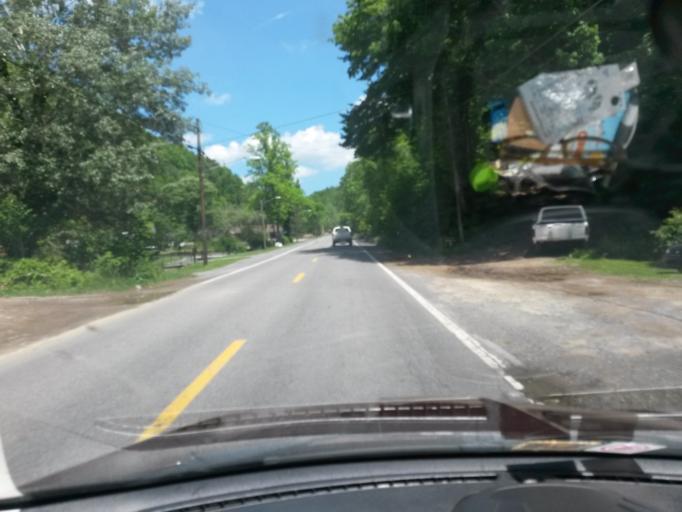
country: US
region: West Virginia
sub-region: McDowell County
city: Welch
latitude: 37.4666
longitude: -81.5410
